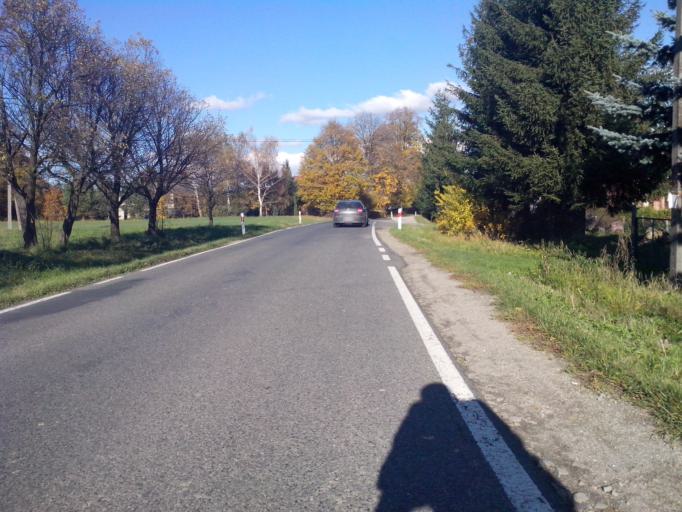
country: PL
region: Subcarpathian Voivodeship
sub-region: Powiat krosnienski
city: Korczyna
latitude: 49.7755
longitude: 21.8523
